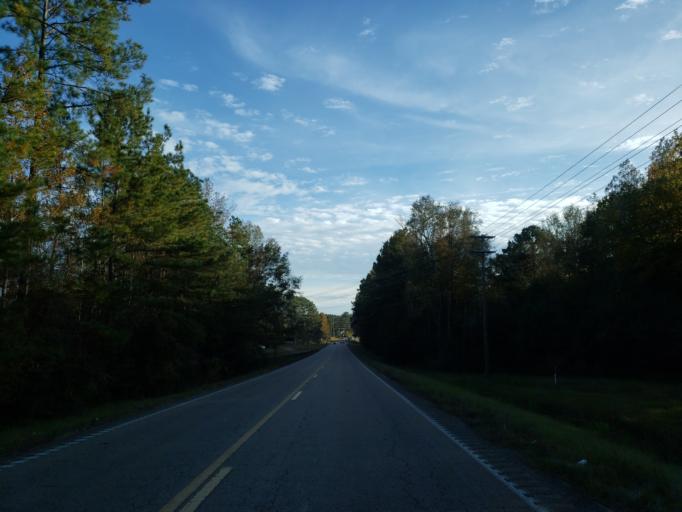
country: US
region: Mississippi
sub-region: Lamar County
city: West Hattiesburg
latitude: 31.3028
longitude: -89.4698
